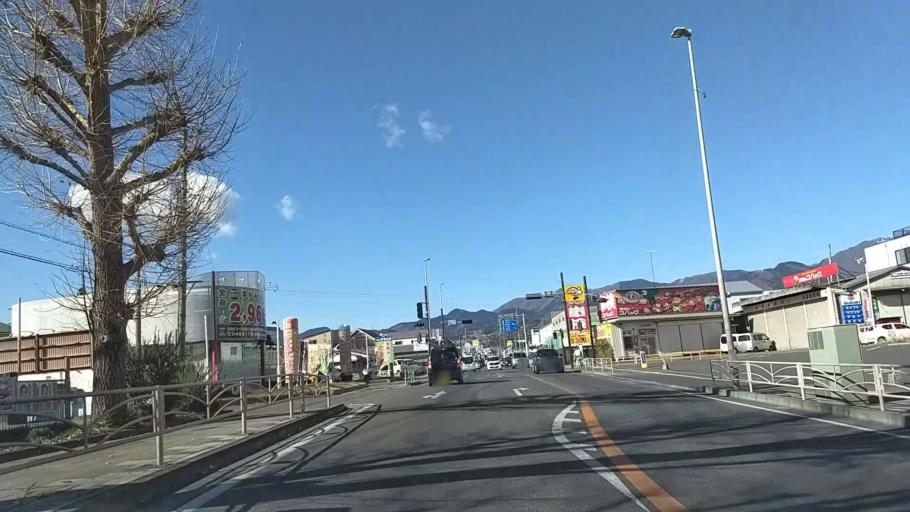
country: JP
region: Kanagawa
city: Hadano
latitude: 35.3718
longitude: 139.1941
